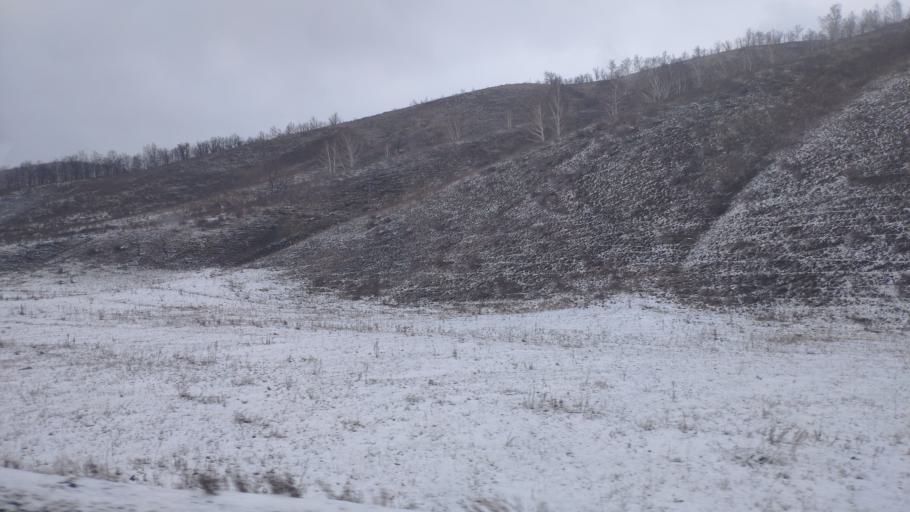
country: RU
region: Bashkortostan
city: Isyangulovo
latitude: 52.1615
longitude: 56.9131
